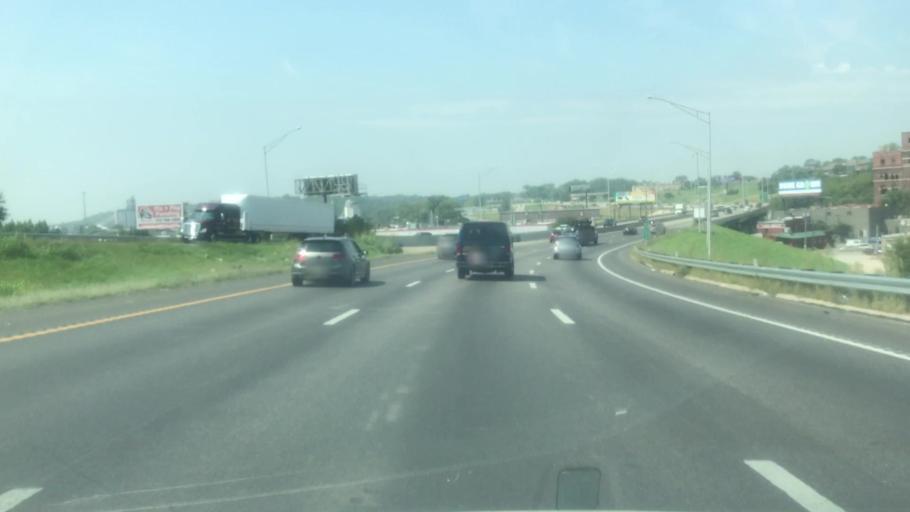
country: US
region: Missouri
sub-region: Jackson County
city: Kansas City
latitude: 39.0758
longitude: -94.5992
